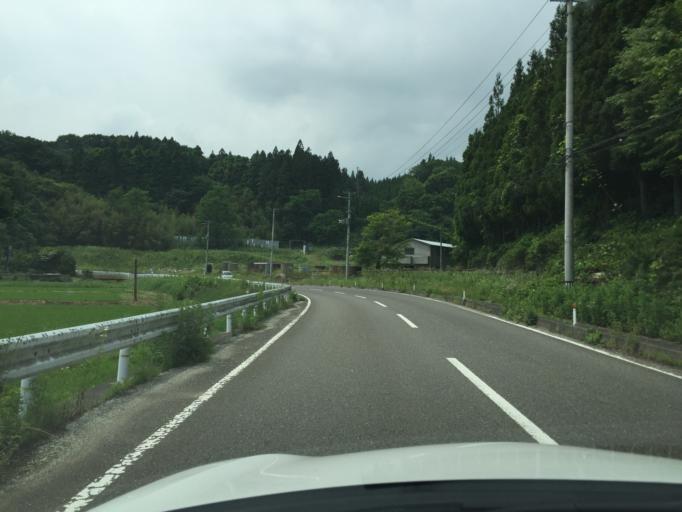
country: JP
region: Fukushima
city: Funehikimachi-funehiki
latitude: 37.2880
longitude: 140.5942
